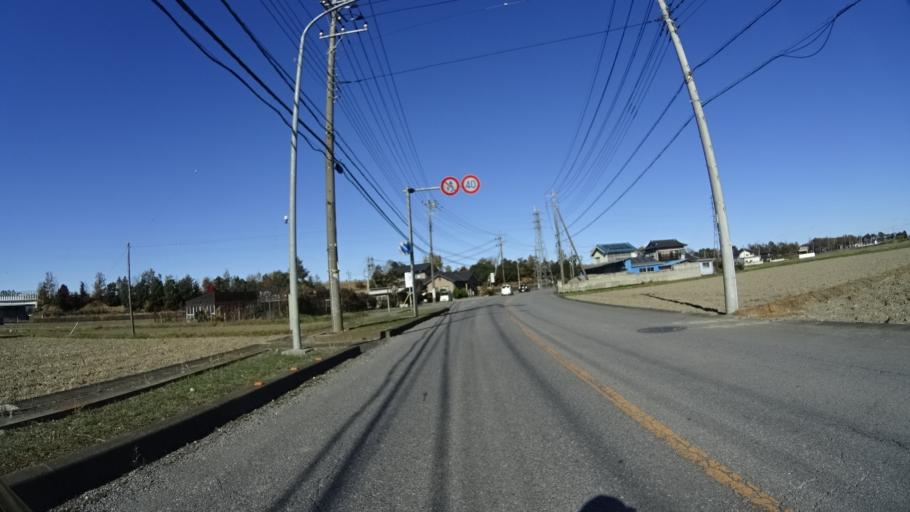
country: JP
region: Tochigi
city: Mibu
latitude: 36.4361
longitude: 139.7502
